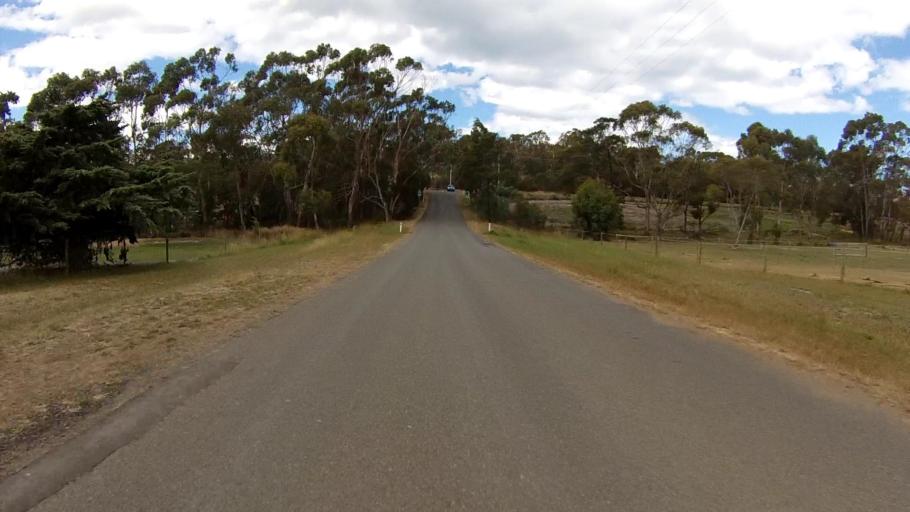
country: AU
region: Tasmania
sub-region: Clarence
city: Acton Park
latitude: -42.8732
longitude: 147.4813
